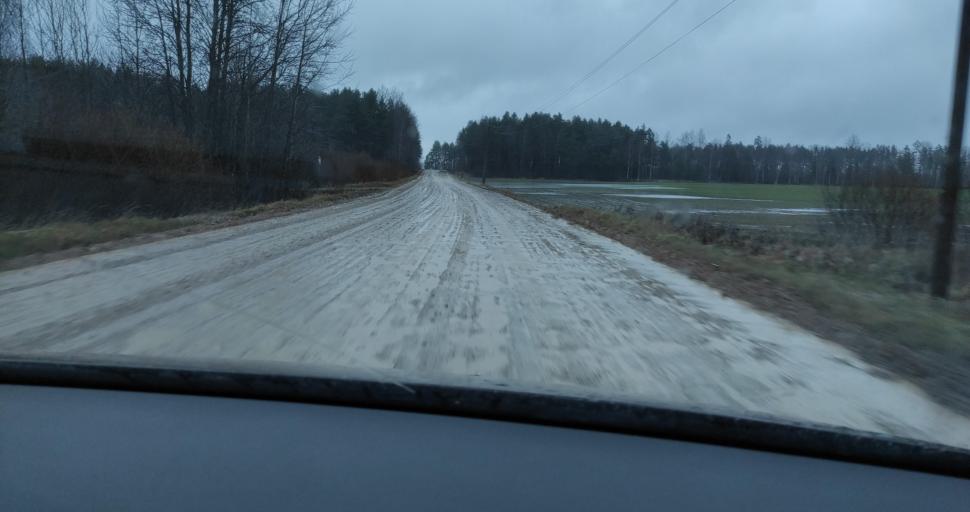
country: LV
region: Skrunda
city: Skrunda
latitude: 56.6833
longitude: 22.2215
